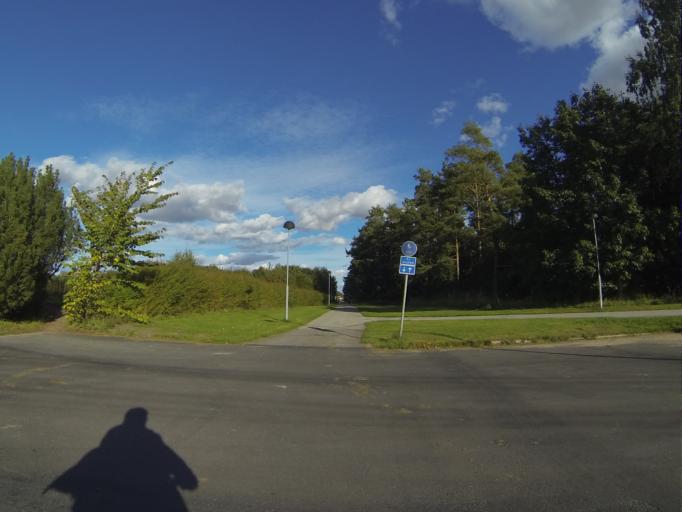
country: SE
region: Skane
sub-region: Lunds Kommun
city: Genarp
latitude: 55.7211
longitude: 13.3505
